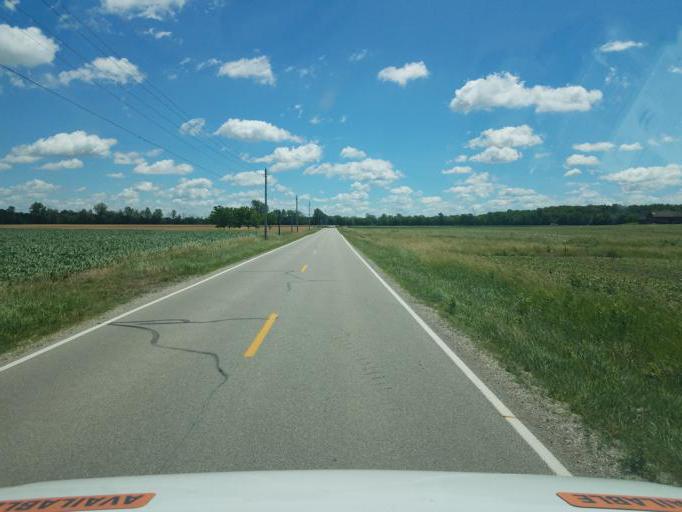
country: US
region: Ohio
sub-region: Crawford County
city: Galion
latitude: 40.7337
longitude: -82.8705
